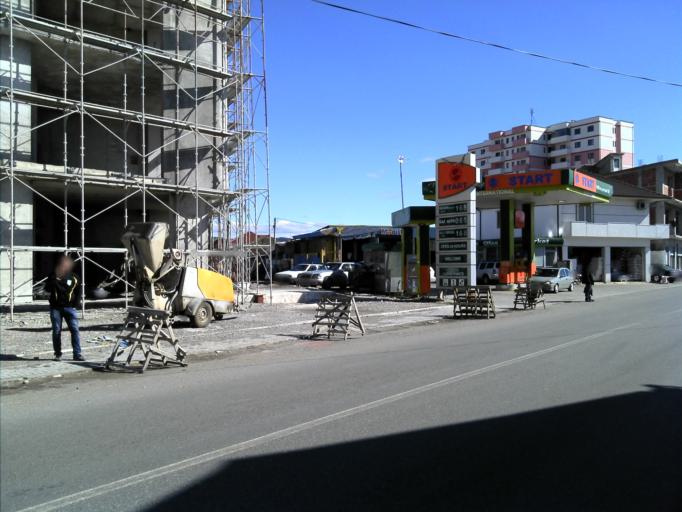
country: AL
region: Shkoder
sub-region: Rrethi i Shkodres
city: Shkoder
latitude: 42.0797
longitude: 19.5138
